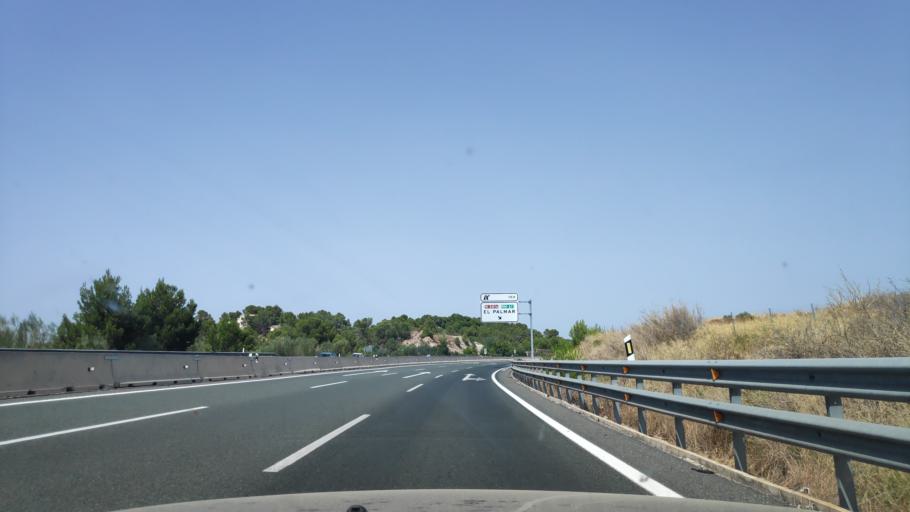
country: ES
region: Murcia
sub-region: Murcia
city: Alcantarilla
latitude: 37.9189
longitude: -1.1629
